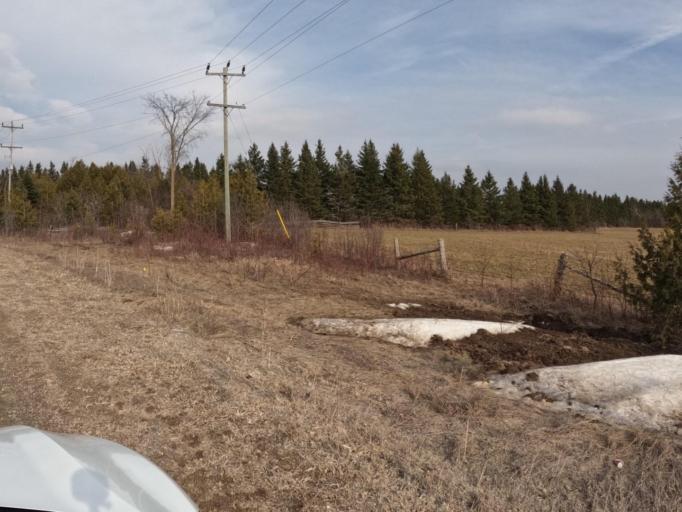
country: CA
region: Ontario
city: Orangeville
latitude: 43.9125
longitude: -80.2636
